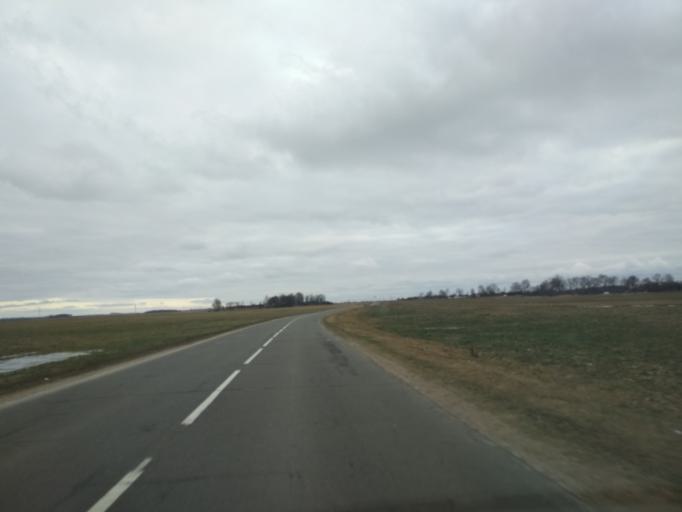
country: BY
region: Minsk
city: Svislach
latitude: 53.5670
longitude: 28.0182
